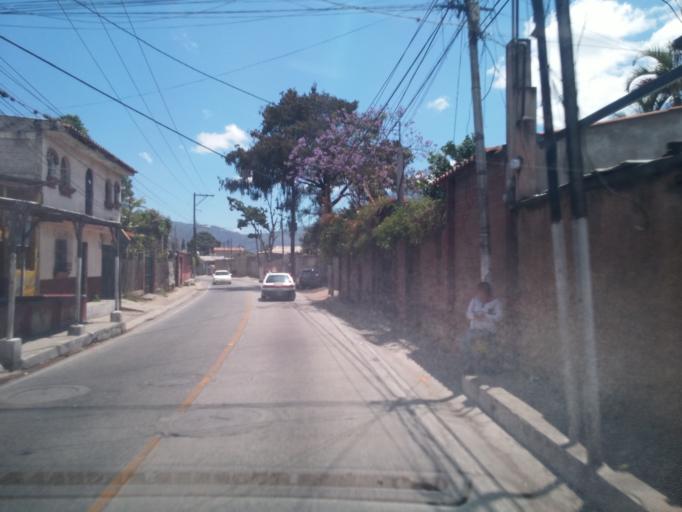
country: GT
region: Sacatepequez
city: Jocotenango
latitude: 14.5810
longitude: -90.7441
